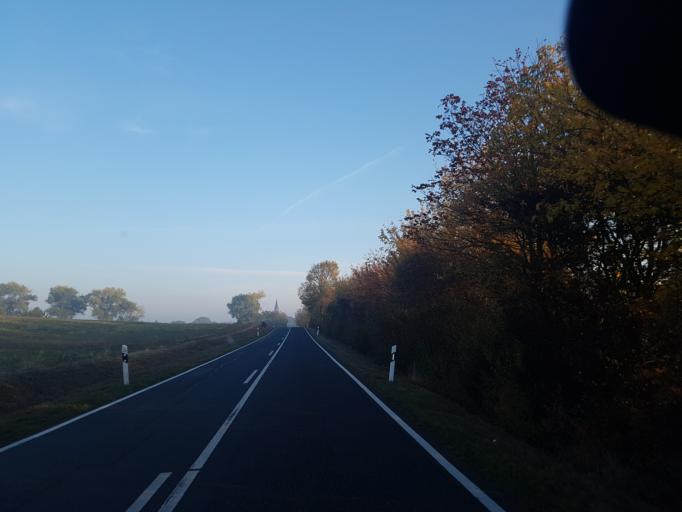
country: DE
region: Brandenburg
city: Juterbog
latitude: 51.9418
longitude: 13.0868
